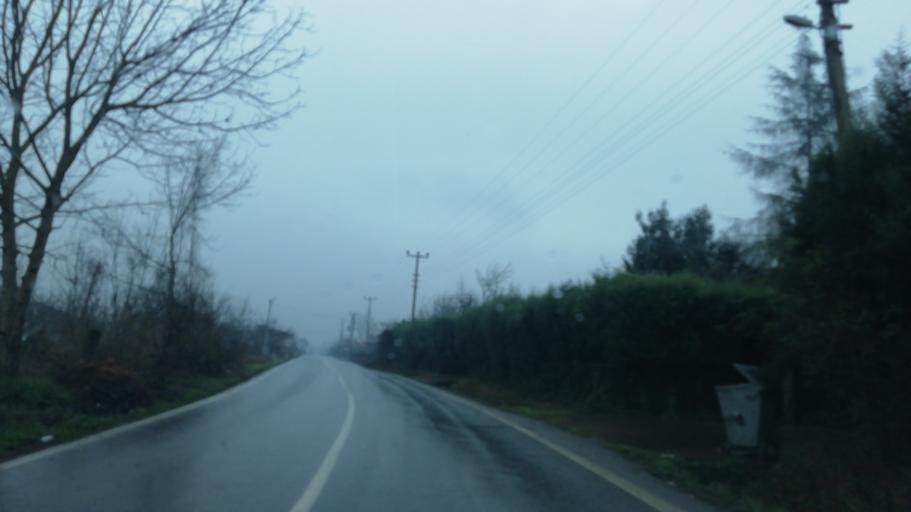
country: TR
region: Sakarya
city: Karapurcek
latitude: 40.6894
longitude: 30.4678
